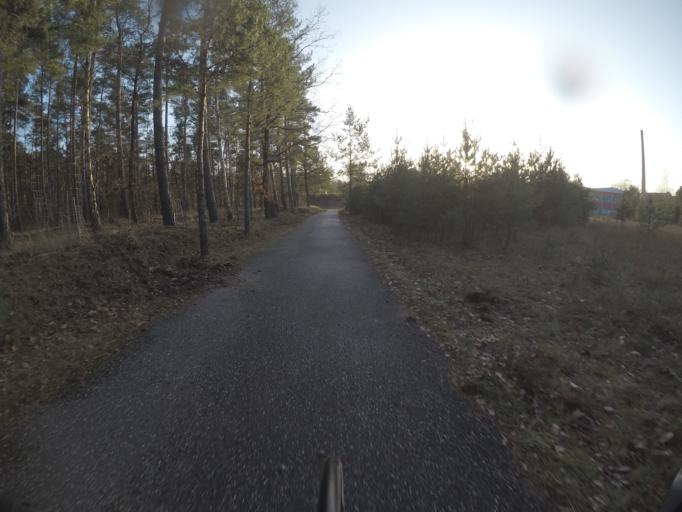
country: DE
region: Brandenburg
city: Hennigsdorf
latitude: 52.6592
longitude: 13.2247
